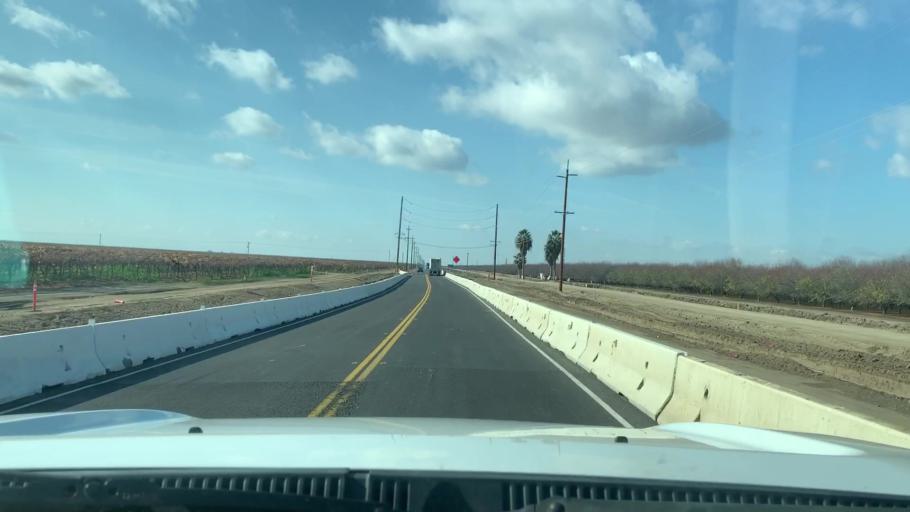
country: US
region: California
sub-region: Kern County
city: McFarland
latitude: 35.6020
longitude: -119.2170
